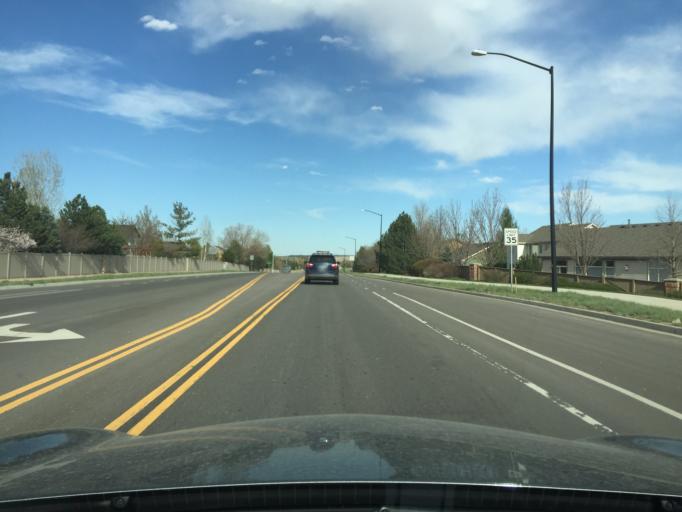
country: US
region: Colorado
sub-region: Boulder County
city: Erie
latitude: 40.0367
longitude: -105.0796
